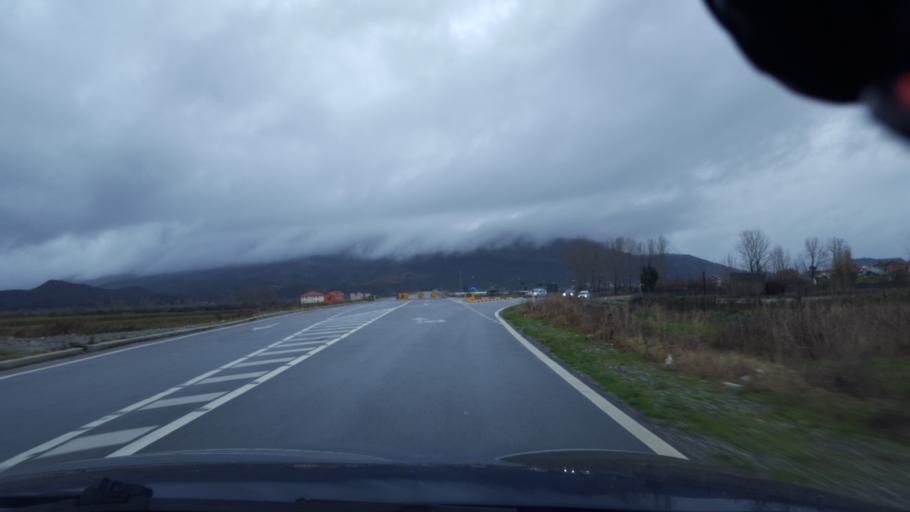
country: AL
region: Shkoder
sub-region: Rrethi i Shkodres
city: Berdica e Madhe
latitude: 42.0050
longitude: 19.4798
